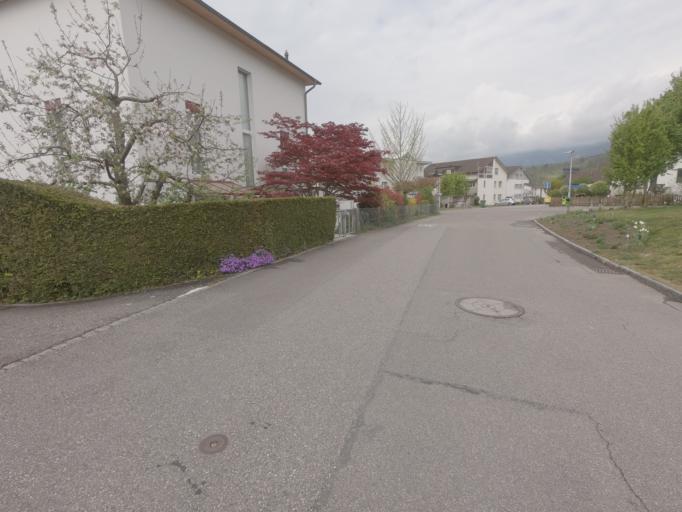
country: CH
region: Solothurn
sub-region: Bezirk Lebern
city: Riedholz
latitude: 47.2190
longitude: 7.5565
